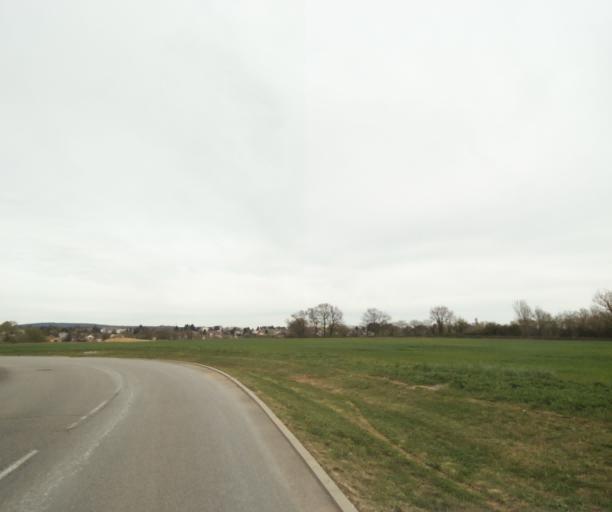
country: FR
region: Bourgogne
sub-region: Departement de Saone-et-Loire
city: Charnay-les-Macon
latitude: 46.2997
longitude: 4.8028
